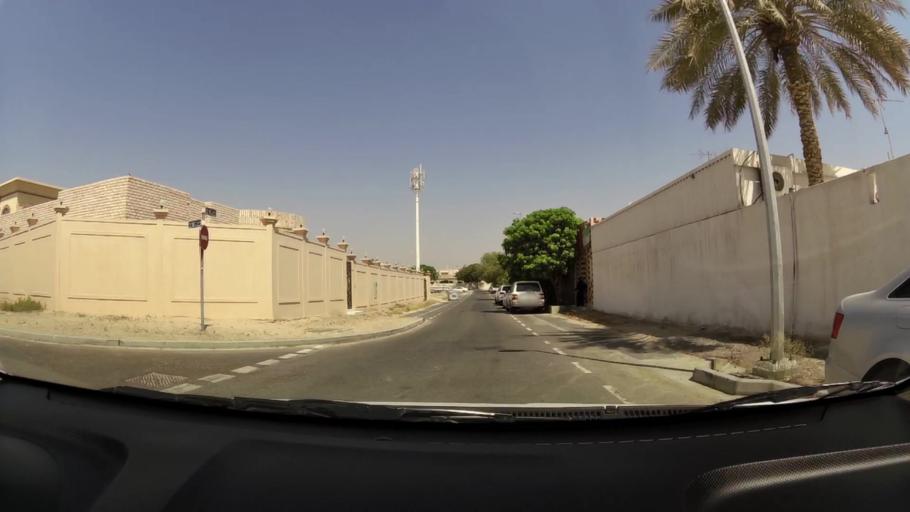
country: AE
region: Ash Shariqah
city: Sharjah
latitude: 25.2729
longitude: 55.3615
